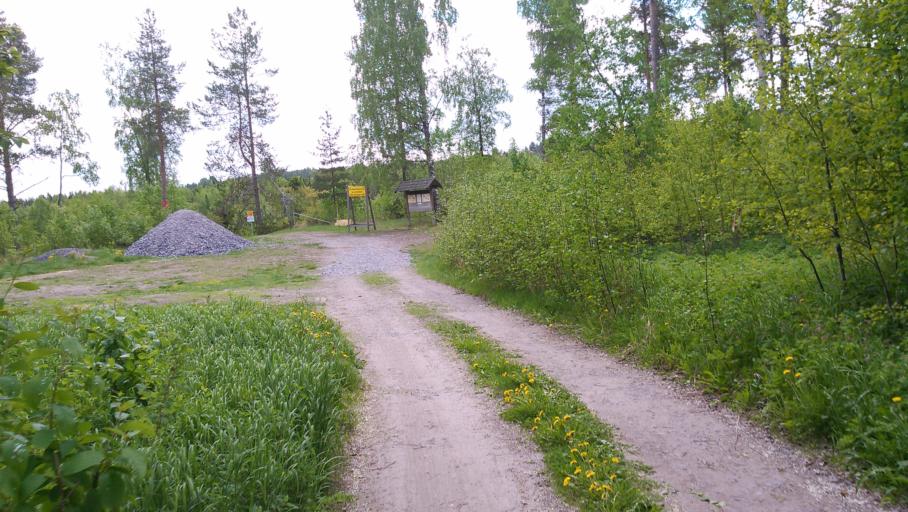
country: SE
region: Vaesterbotten
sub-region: Umea Kommun
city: Roback
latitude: 63.8803
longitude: 20.0242
